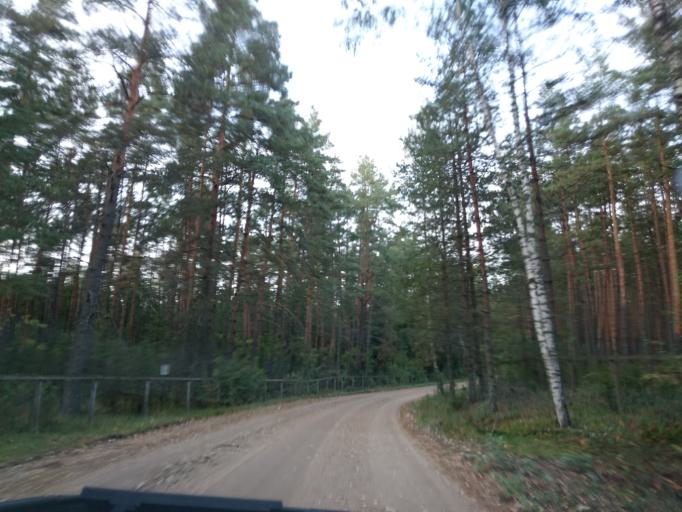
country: LV
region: Garkalne
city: Garkalne
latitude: 57.0456
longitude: 24.3839
